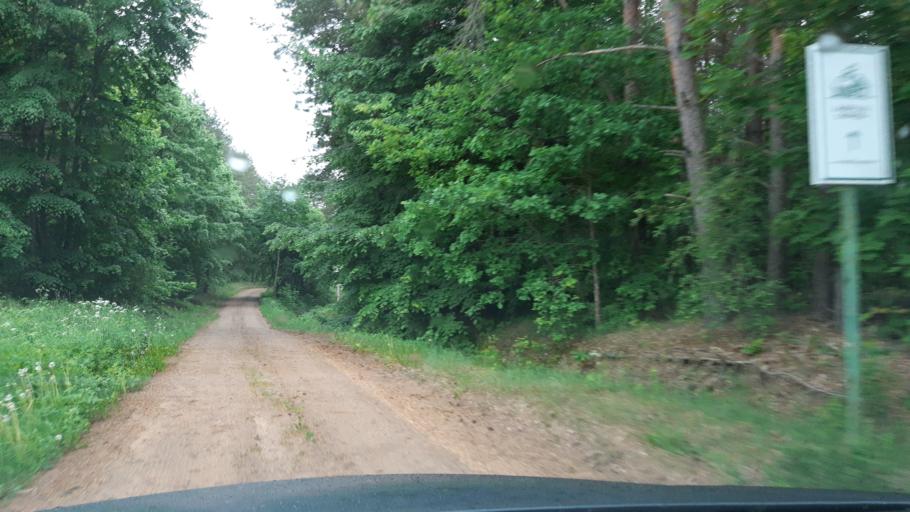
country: LT
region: Utenos apskritis
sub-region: Anyksciai
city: Anyksciai
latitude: 55.4484
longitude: 25.2081
